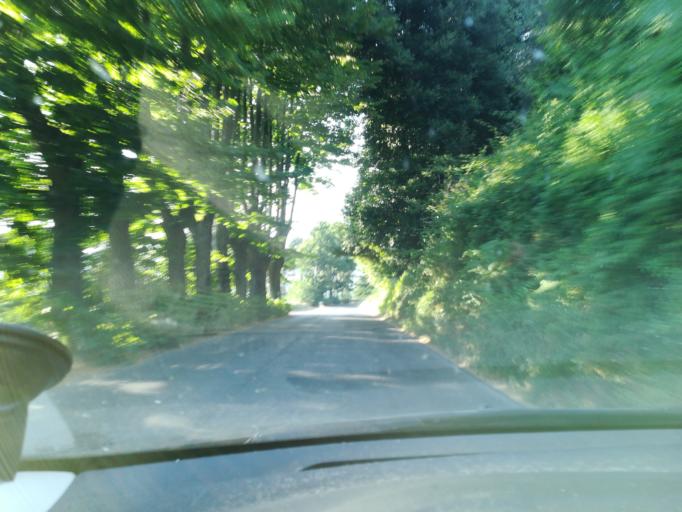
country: IT
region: Tuscany
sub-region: Provincia di Lucca
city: Stiava
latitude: 43.9167
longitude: 10.3392
